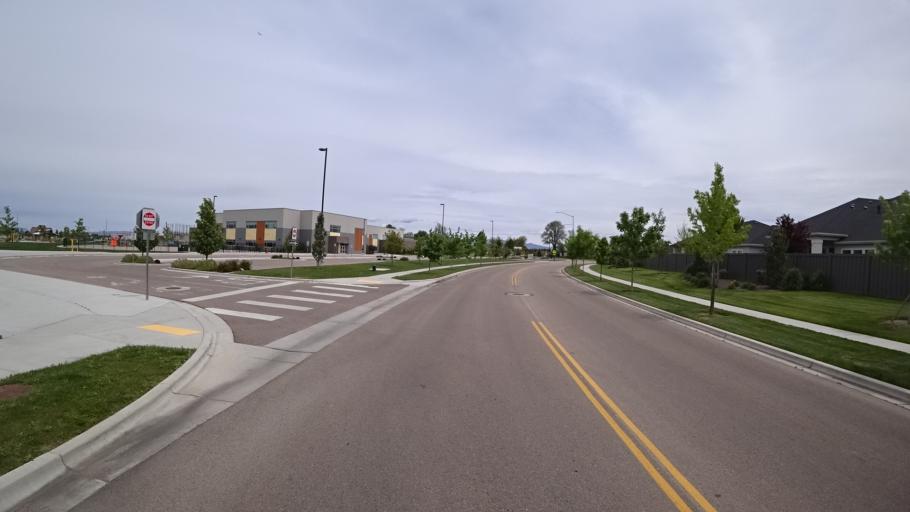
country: US
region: Idaho
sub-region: Ada County
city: Meridian
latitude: 43.5564
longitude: -116.3470
